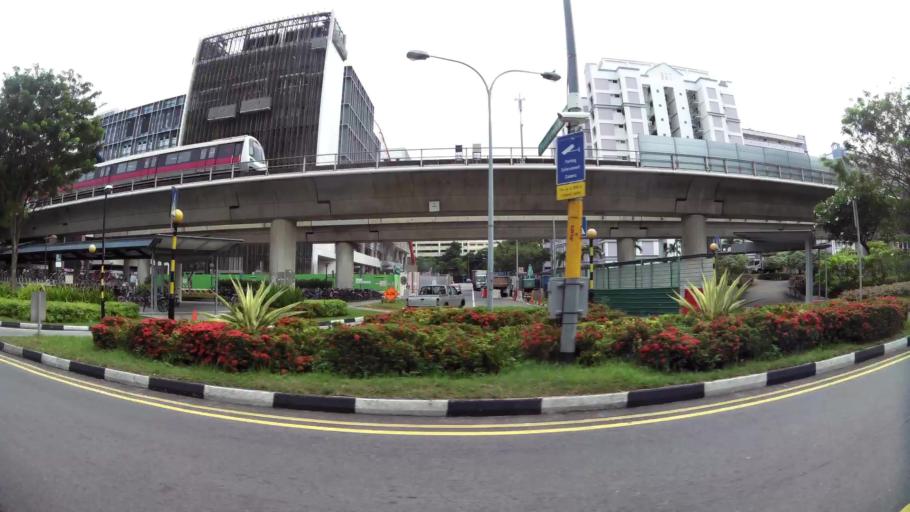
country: MY
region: Johor
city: Johor Bahru
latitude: 1.4404
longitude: 103.7998
